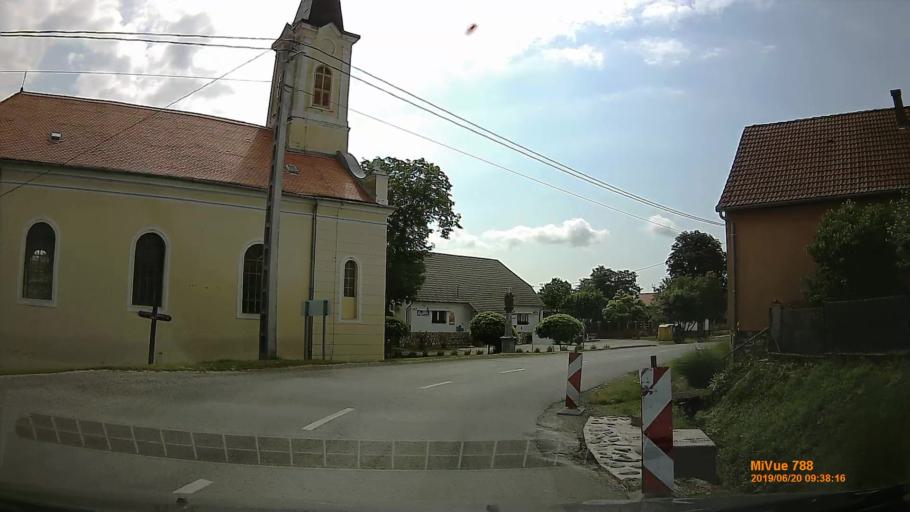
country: HU
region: Baranya
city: Pecsvarad
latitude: 46.1573
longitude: 18.4729
